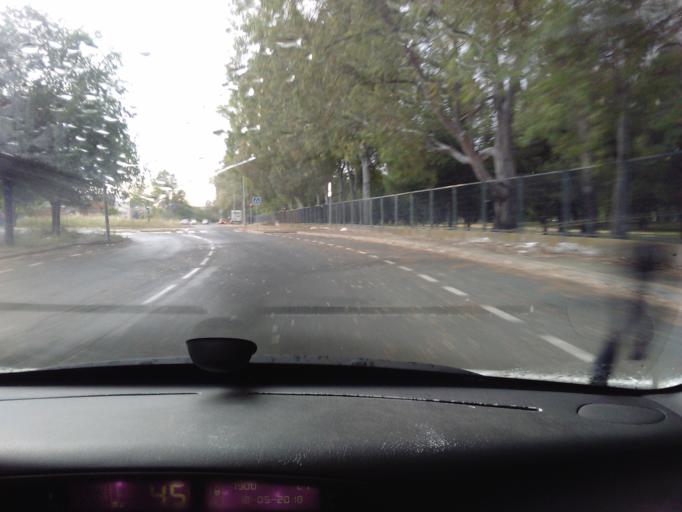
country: ES
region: Andalusia
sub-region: Provincia de Sevilla
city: Sevilla
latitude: 37.3960
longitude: -5.9386
